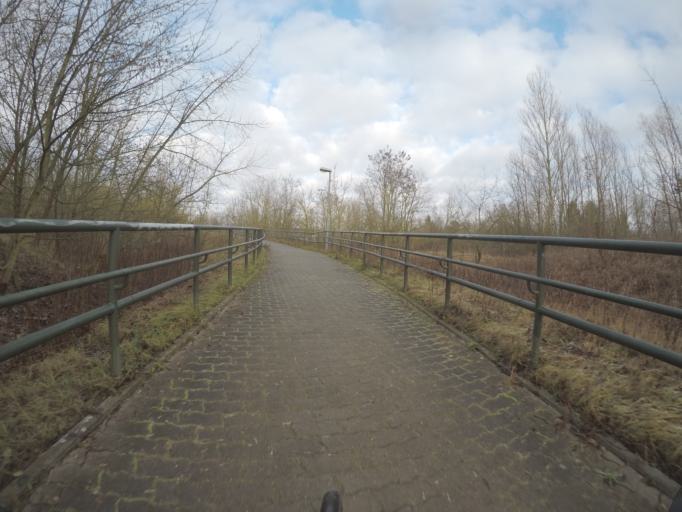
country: DE
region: Berlin
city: Stadtrandsiedlung Malchow
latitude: 52.5797
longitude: 13.4938
